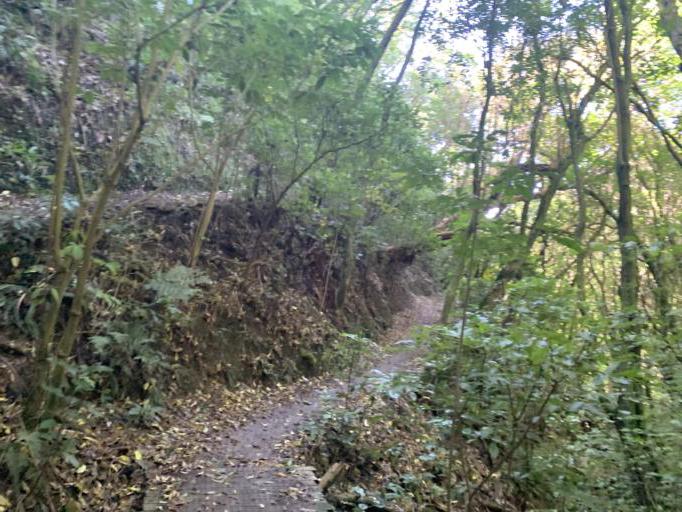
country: NZ
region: Wellington
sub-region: Wellington City
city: Brooklyn
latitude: -41.3006
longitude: 174.7528
